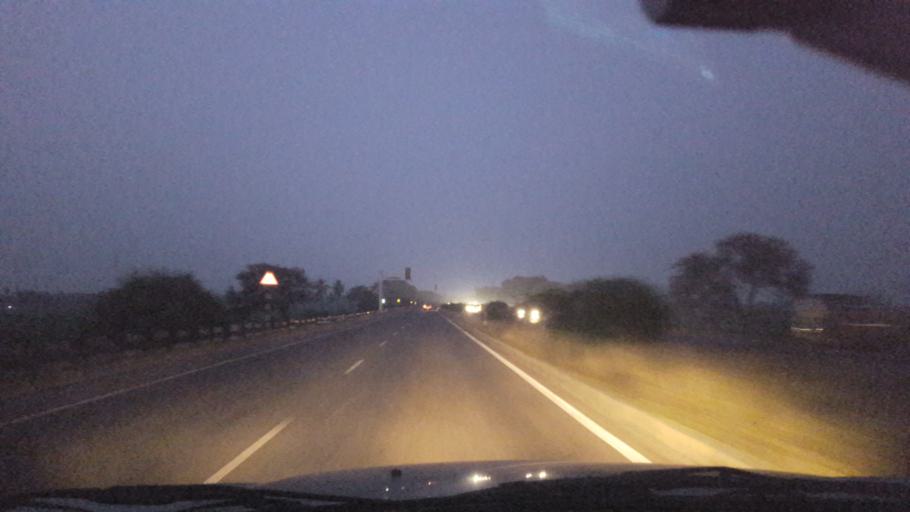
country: IN
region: Andhra Pradesh
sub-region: East Godavari
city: Rajahmundry
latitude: 17.1130
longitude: 81.9239
